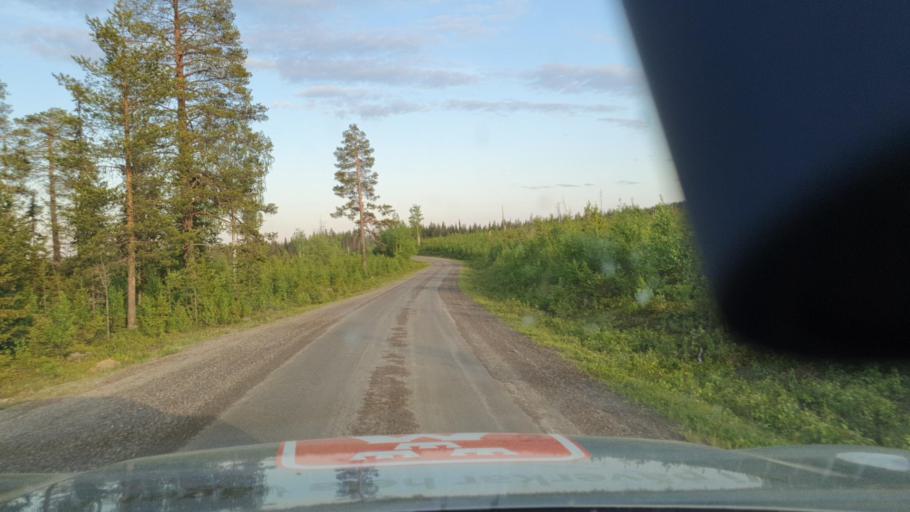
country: SE
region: Norrbotten
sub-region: Bodens Kommun
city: Boden
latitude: 66.4693
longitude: 21.6320
